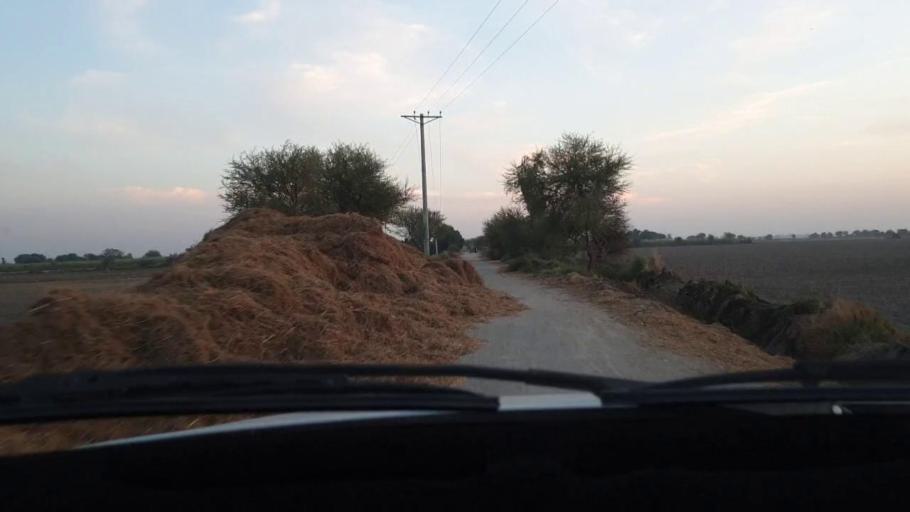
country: PK
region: Sindh
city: Tando Muhammad Khan
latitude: 25.0870
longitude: 68.3967
